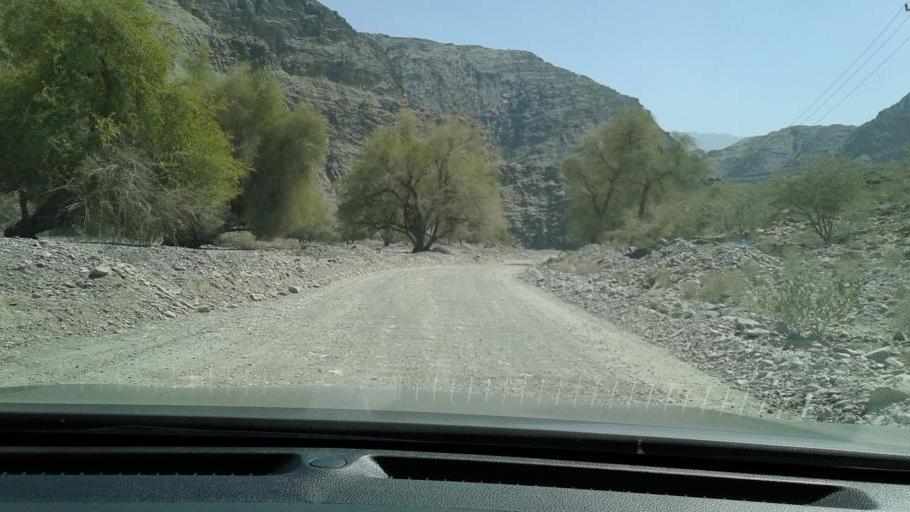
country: OM
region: Al Batinah
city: Bayt al `Awabi
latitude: 23.2611
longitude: 57.4420
